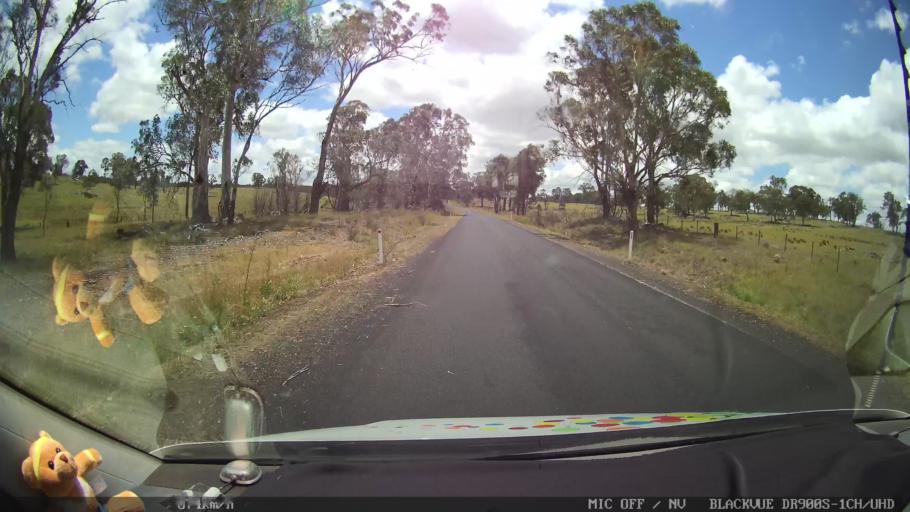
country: AU
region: New South Wales
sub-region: Glen Innes Severn
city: Glen Innes
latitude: -29.4370
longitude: 151.7691
